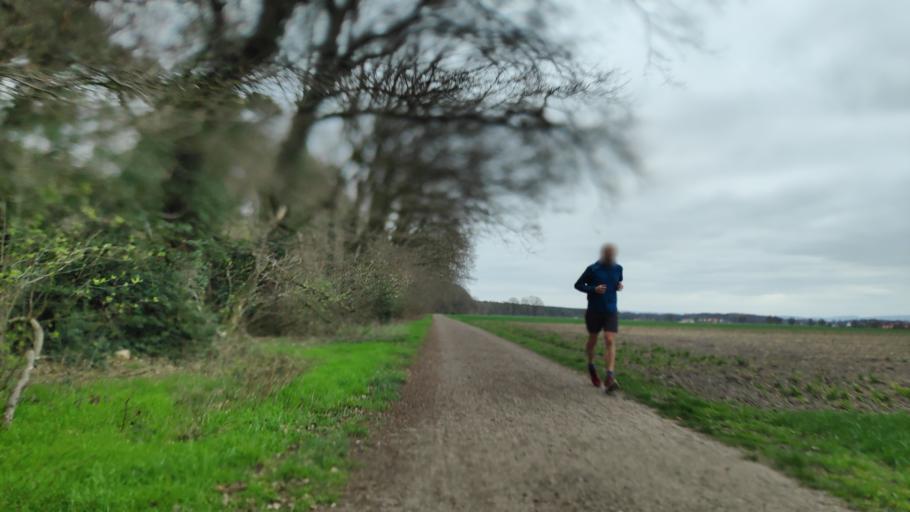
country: DE
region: North Rhine-Westphalia
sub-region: Regierungsbezirk Detmold
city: Petershagen
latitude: 52.3593
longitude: 8.9186
